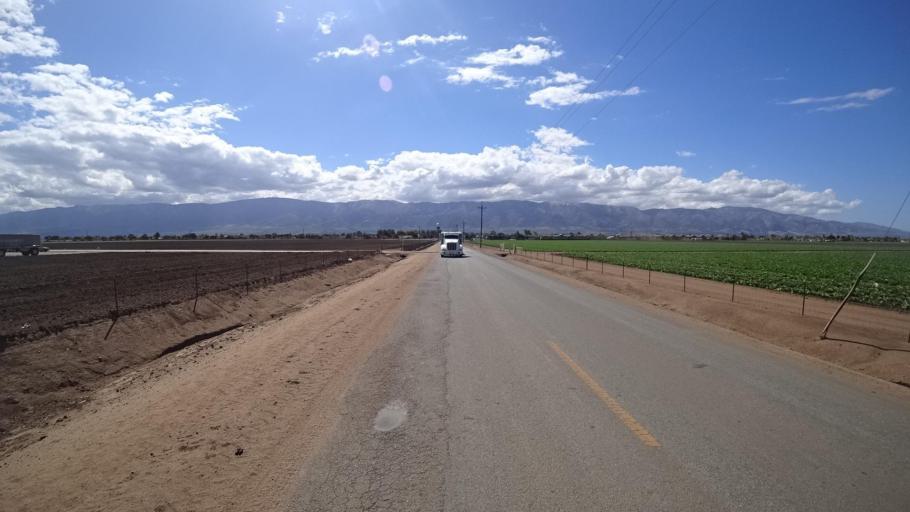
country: US
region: California
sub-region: Monterey County
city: Gonzales
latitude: 36.5164
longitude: -121.4291
